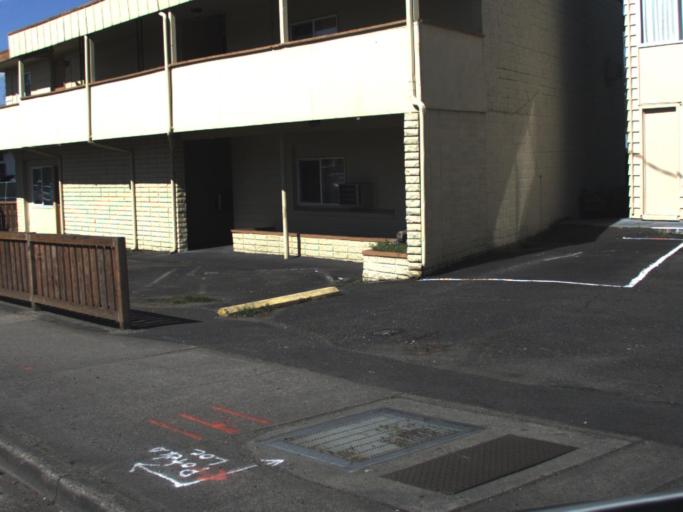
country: US
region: Washington
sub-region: King County
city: Auburn
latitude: 47.2969
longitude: -122.2172
